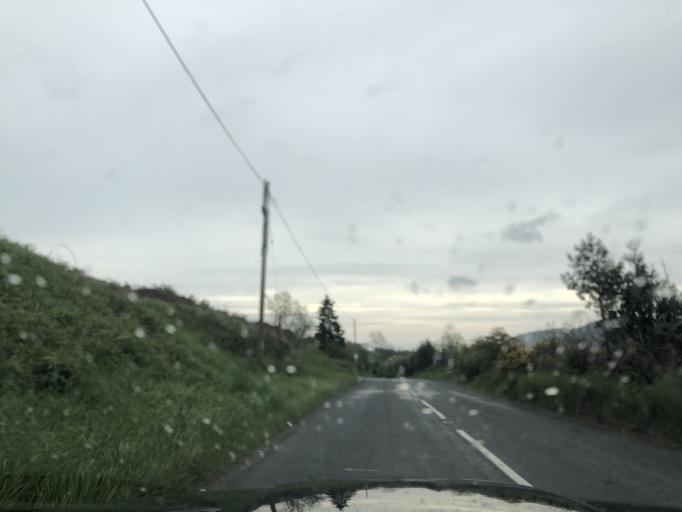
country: GB
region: Northern Ireland
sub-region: Down District
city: Castlewellan
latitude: 54.2226
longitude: -5.9755
